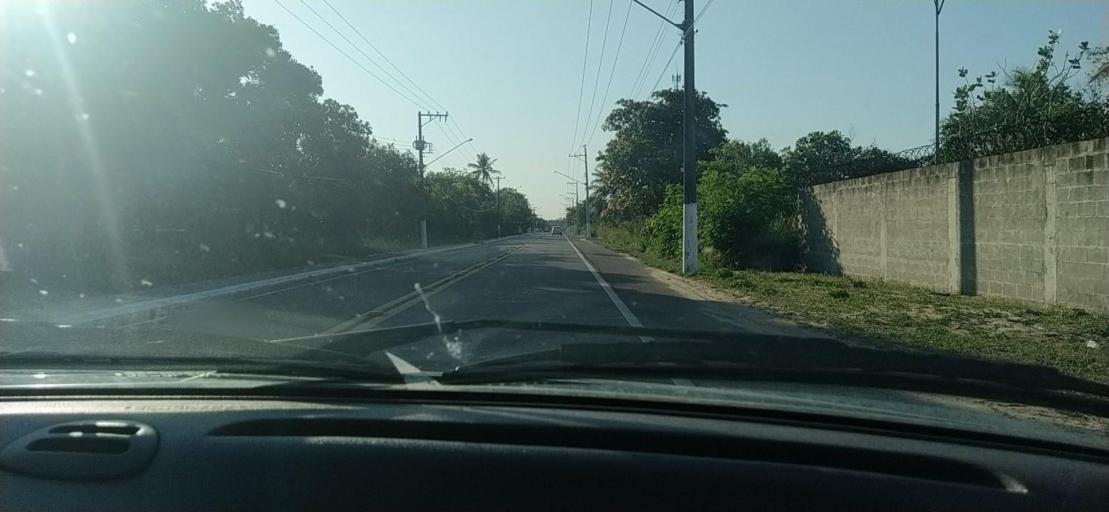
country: BR
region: Espirito Santo
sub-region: Conceicao Da Barra
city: Conceicao da Barra
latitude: -18.5730
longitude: -39.7360
